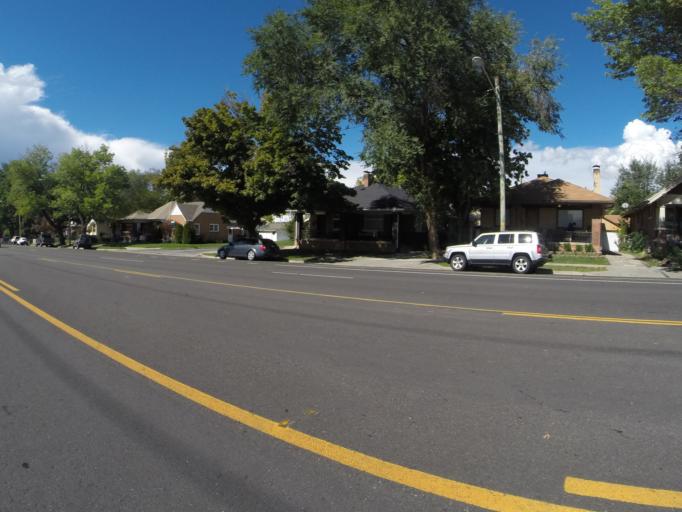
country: US
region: Utah
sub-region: Salt Lake County
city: Salt Lake City
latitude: 40.7520
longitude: -111.8664
